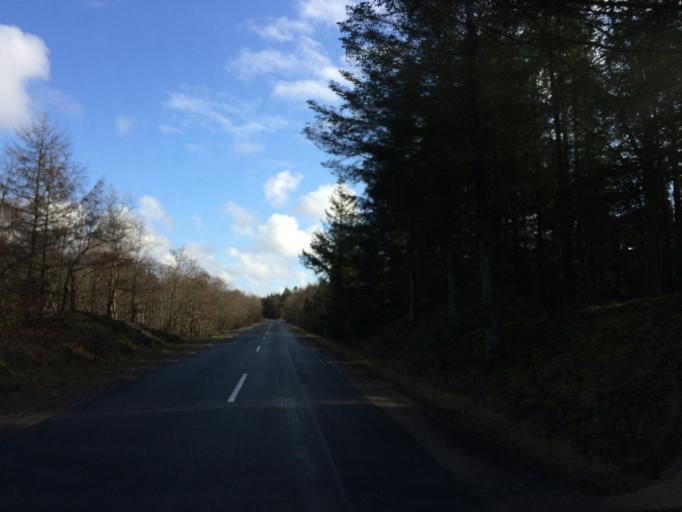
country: DK
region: Central Jutland
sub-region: Holstebro Kommune
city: Ulfborg
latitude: 56.2640
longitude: 8.3384
